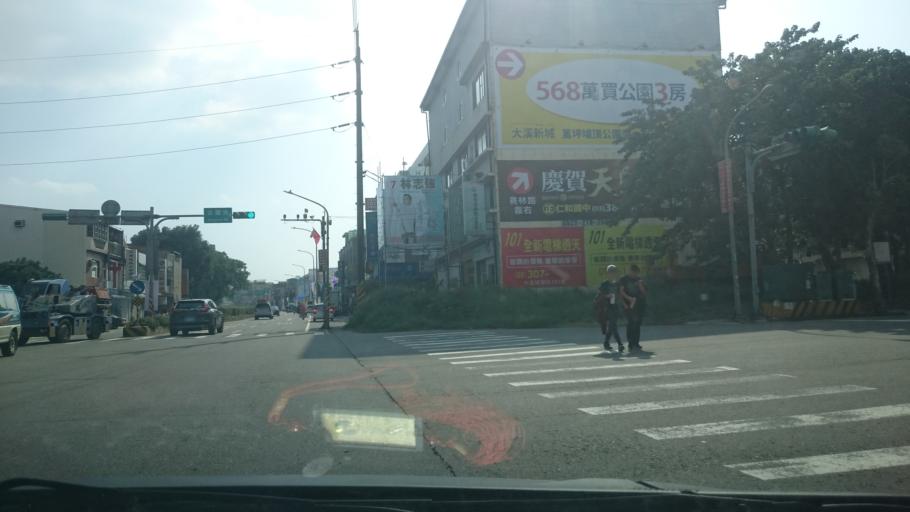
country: TW
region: Taiwan
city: Daxi
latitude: 24.9046
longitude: 121.2847
